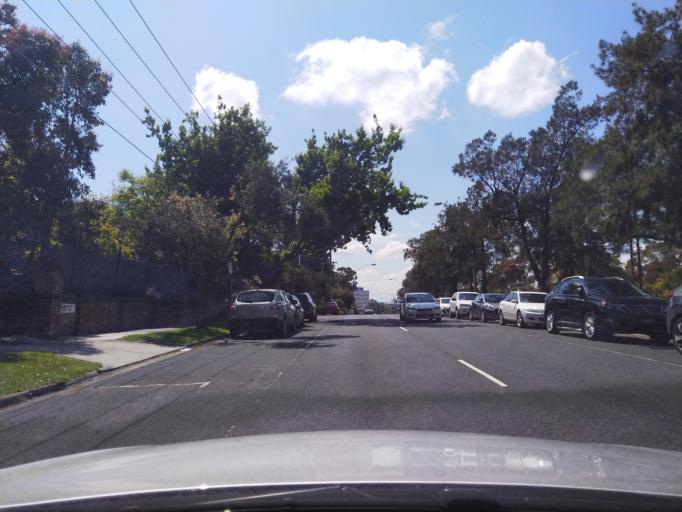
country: AU
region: Victoria
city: Rosanna
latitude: -37.7599
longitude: 145.0569
